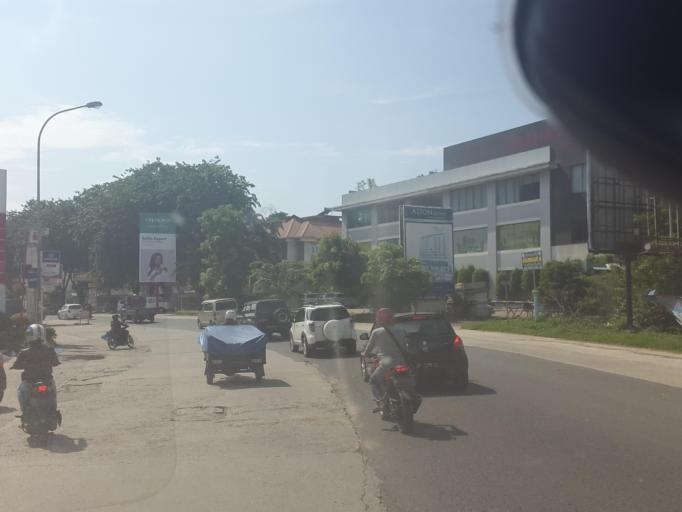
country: SG
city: Singapore
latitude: 1.1419
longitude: 104.0215
